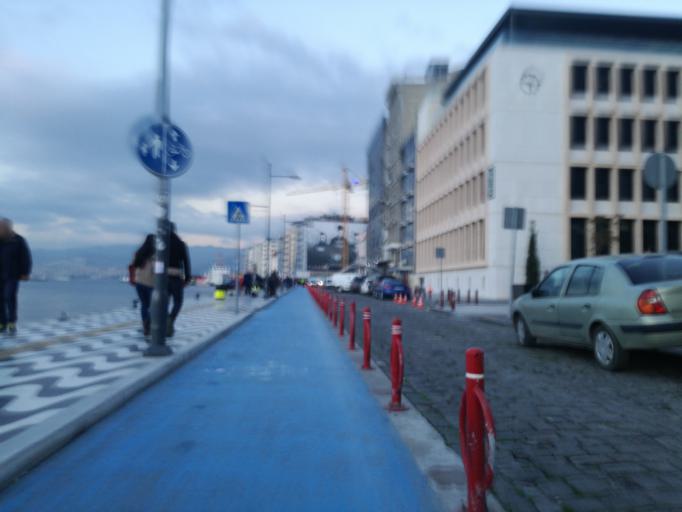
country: TR
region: Izmir
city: Izmir
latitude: 38.4232
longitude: 27.1307
